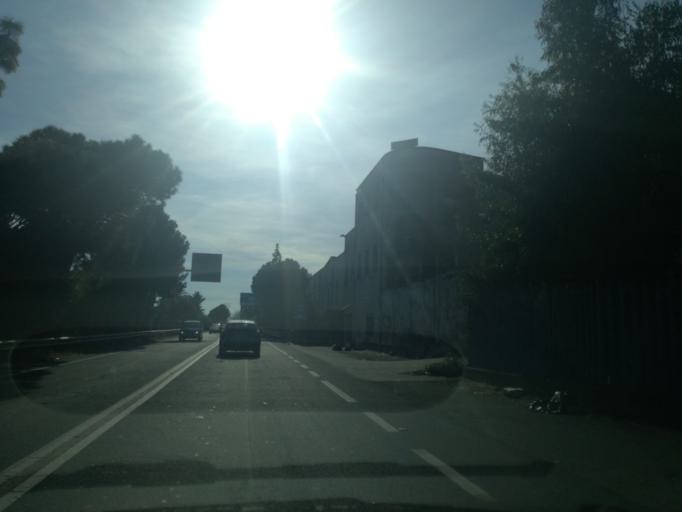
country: IT
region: Sicily
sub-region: Catania
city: Acireale
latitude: 37.6005
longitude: 15.1677
